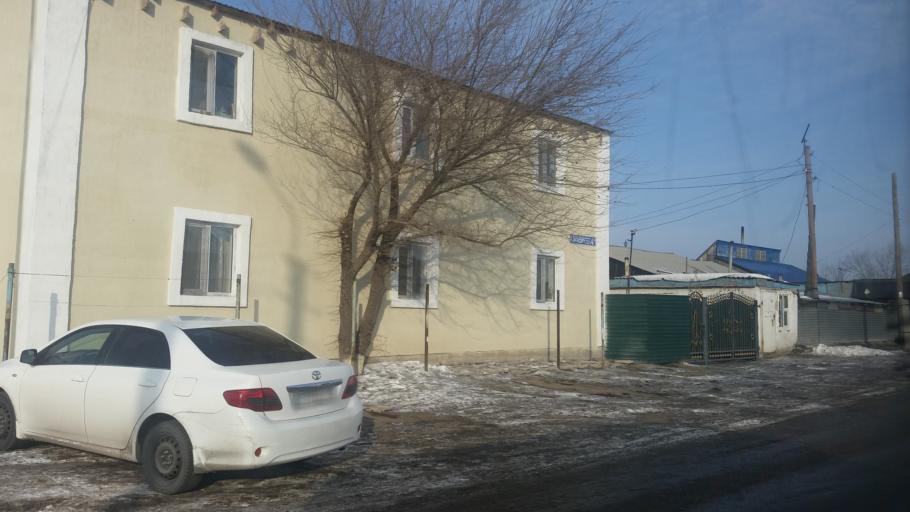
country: KZ
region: Astana Qalasy
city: Astana
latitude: 51.1862
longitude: 71.3965
